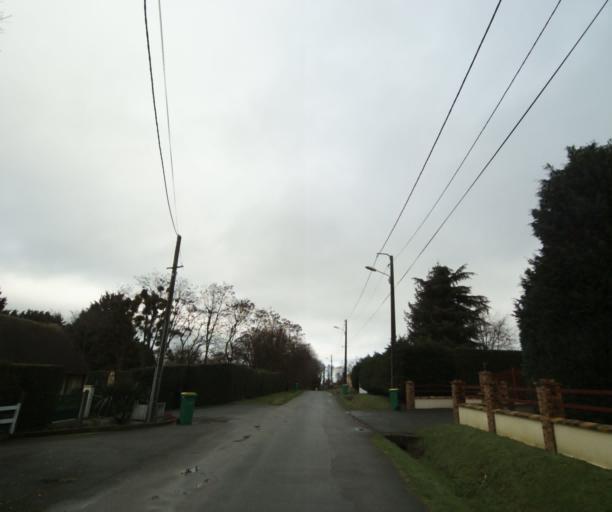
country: FR
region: Pays de la Loire
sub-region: Departement de la Sarthe
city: La Chapelle-Saint-Aubin
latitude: 48.0251
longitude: 0.1445
